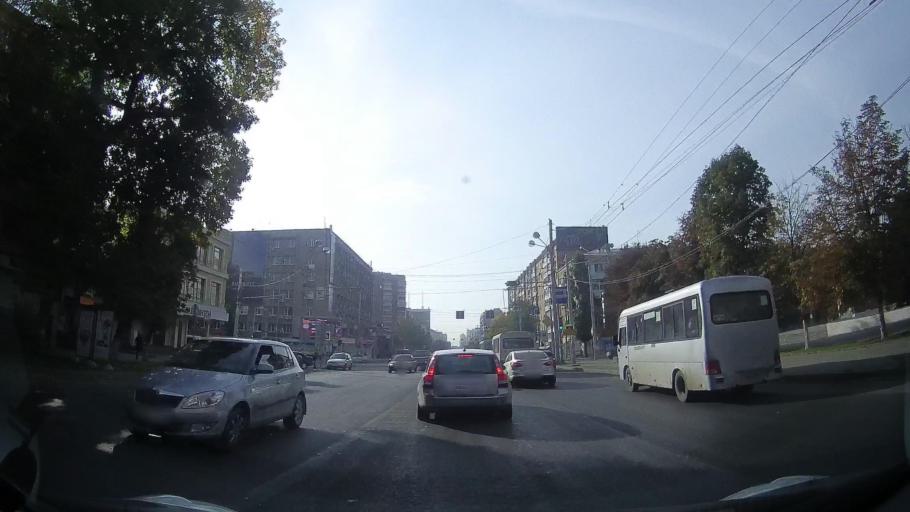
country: RU
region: Rostov
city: Rostov-na-Donu
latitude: 47.2292
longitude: 39.7158
